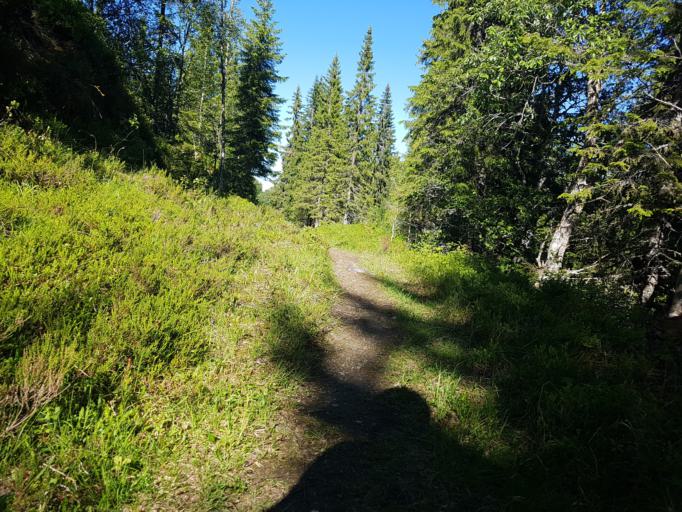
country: NO
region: Sor-Trondelag
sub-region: Trondheim
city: Trondheim
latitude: 63.4354
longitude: 10.2733
